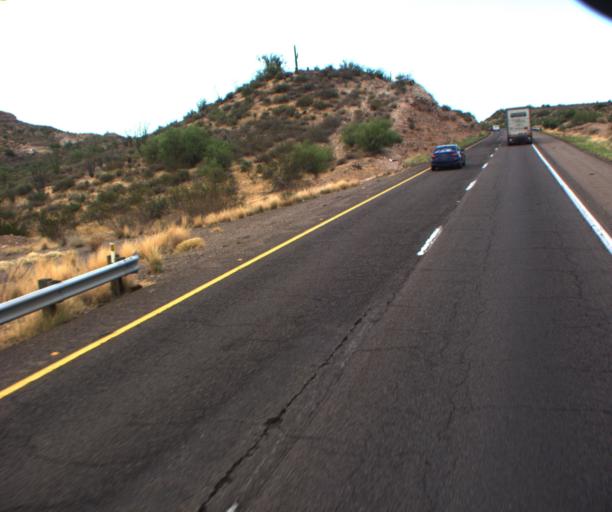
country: US
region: Arizona
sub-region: Maricopa County
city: New River
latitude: 33.9932
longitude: -112.1372
